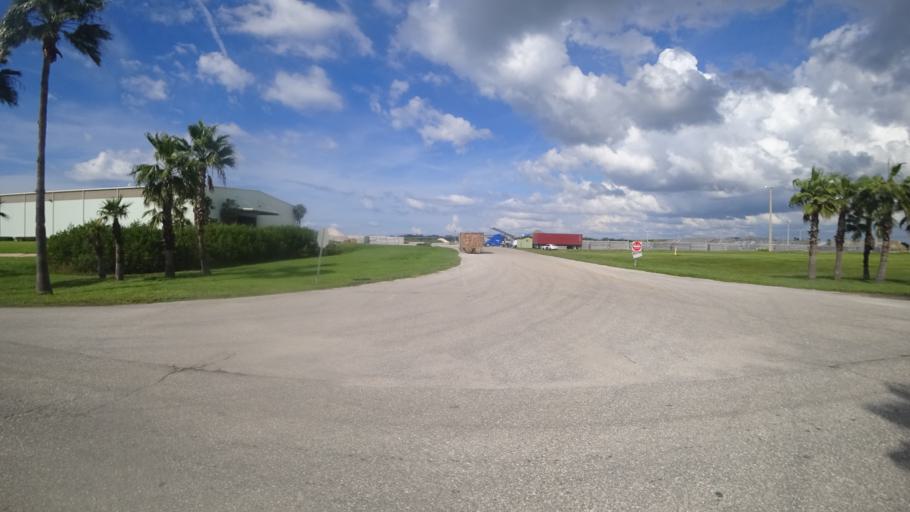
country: US
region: Florida
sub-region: Manatee County
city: Memphis
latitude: 27.6313
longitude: -82.5516
